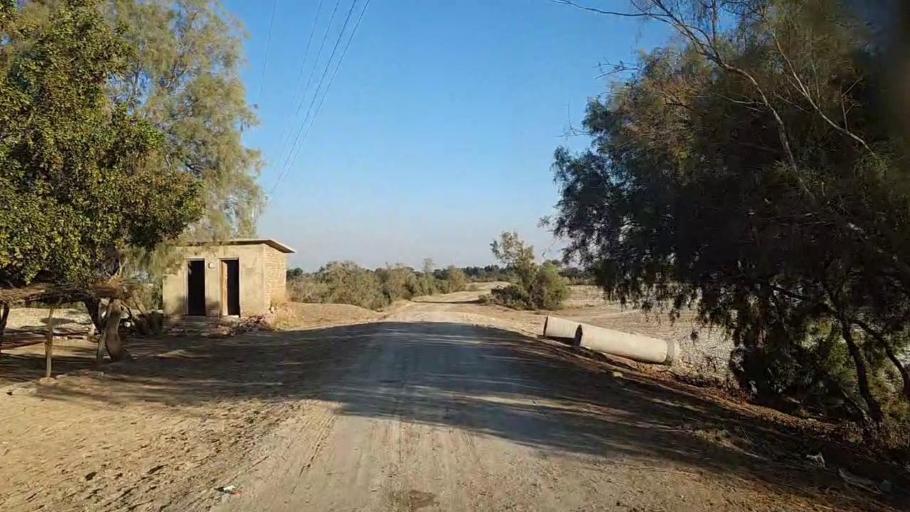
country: PK
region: Sindh
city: Khairpur
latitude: 27.8878
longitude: 69.7098
